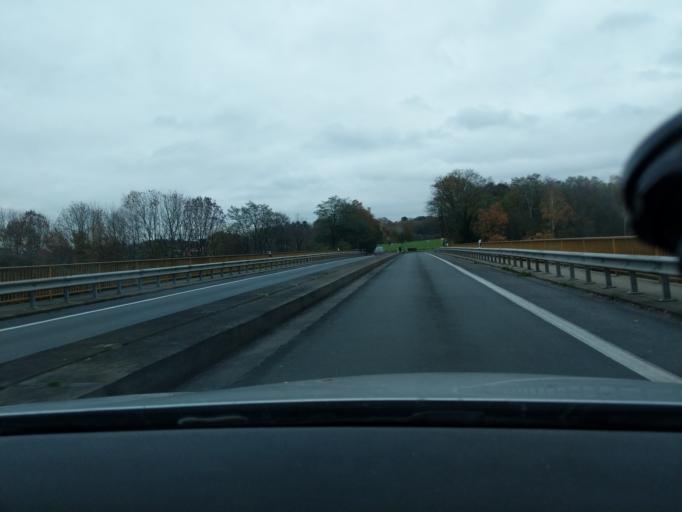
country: DE
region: North Rhine-Westphalia
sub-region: Regierungsbezirk Munster
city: Horstel
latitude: 52.2807
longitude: 7.6043
